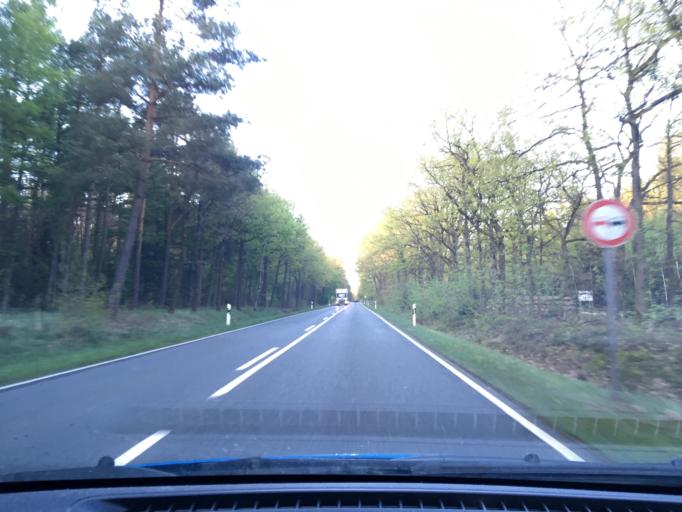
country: DE
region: Lower Saxony
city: Soderstorf
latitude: 53.0855
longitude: 10.0912
